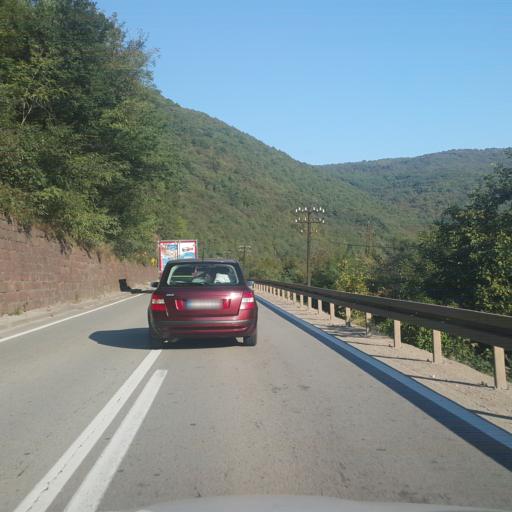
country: RS
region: Central Serbia
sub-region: Nisavski Okrug
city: Niska Banja
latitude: 43.3174
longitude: 22.0529
